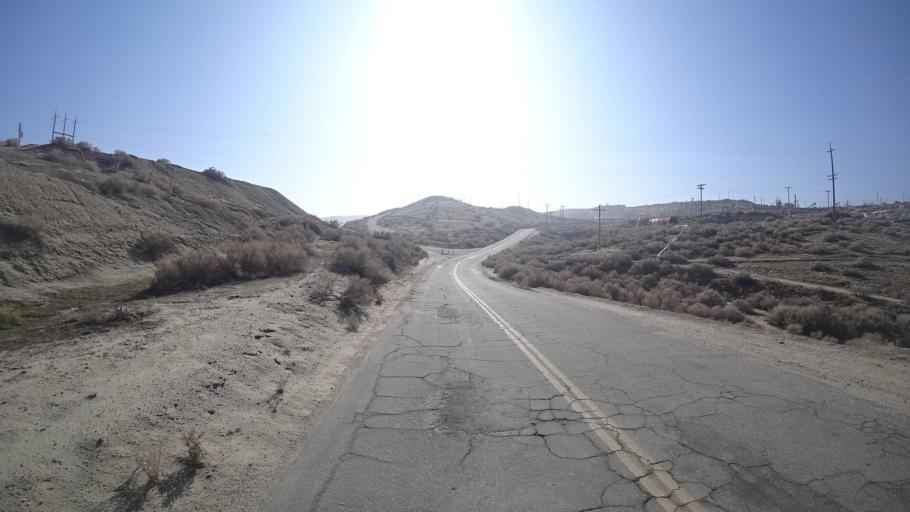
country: US
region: California
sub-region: Kern County
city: Taft Heights
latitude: 35.1235
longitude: -119.4723
